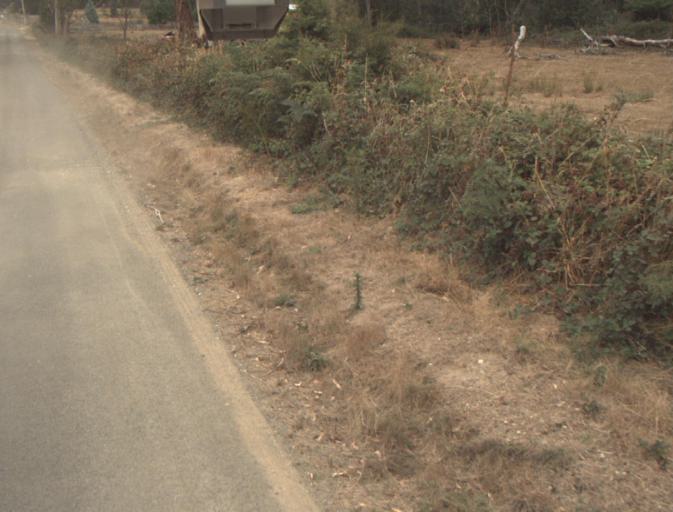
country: AU
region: Tasmania
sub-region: Dorset
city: Bridport
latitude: -41.1743
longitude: 147.2663
